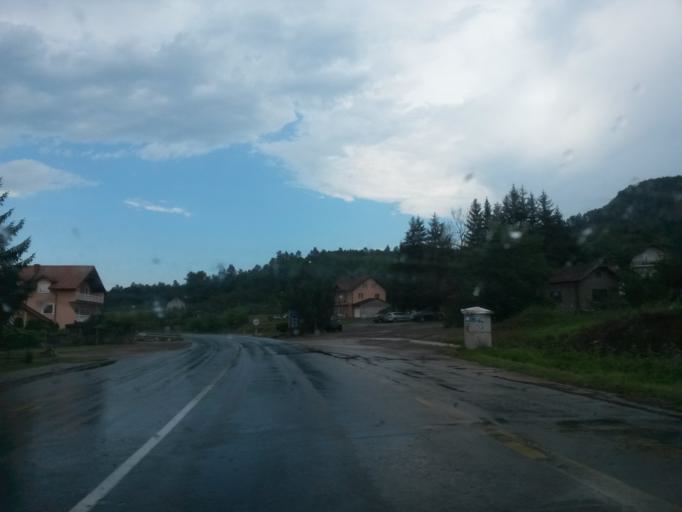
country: BA
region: Federation of Bosnia and Herzegovina
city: Lijesnica
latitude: 44.4909
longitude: 18.0849
